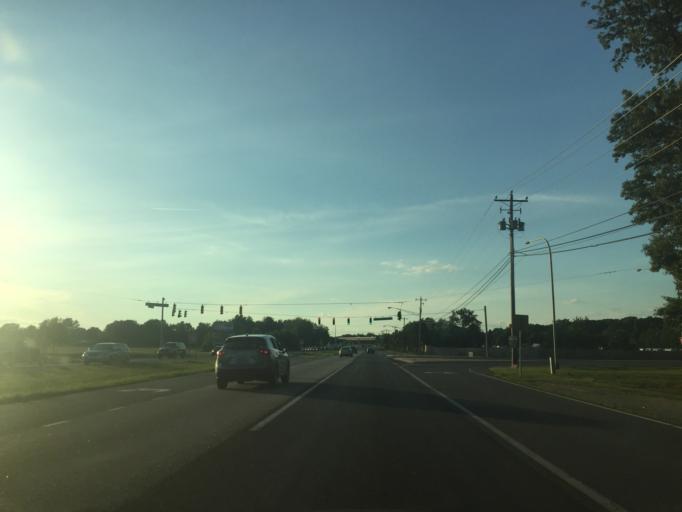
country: US
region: Delaware
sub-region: Kent County
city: Smyrna
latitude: 39.3240
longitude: -75.6211
